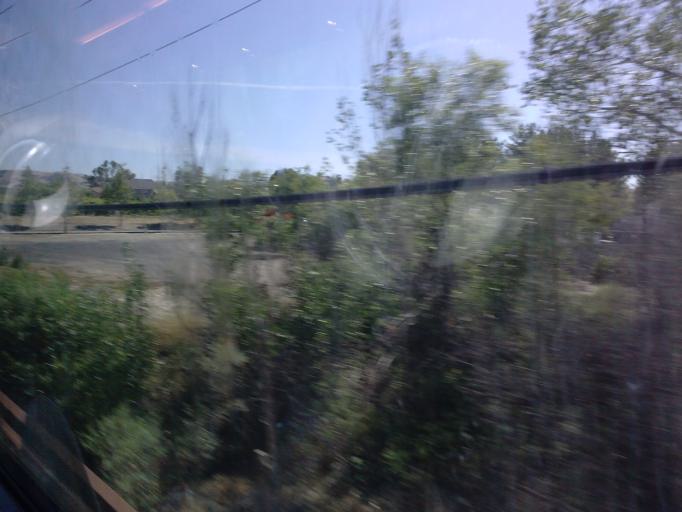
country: US
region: California
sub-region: Alameda County
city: Livermore
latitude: 37.6673
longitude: -121.7499
